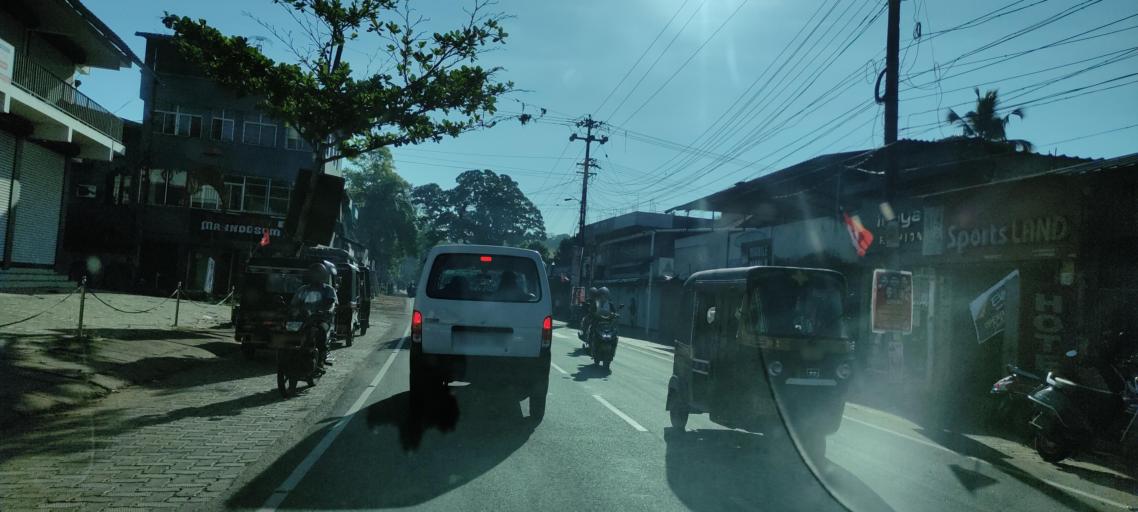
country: IN
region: Kerala
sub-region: Alappuzha
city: Kattanam
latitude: 9.1754
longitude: 76.6165
